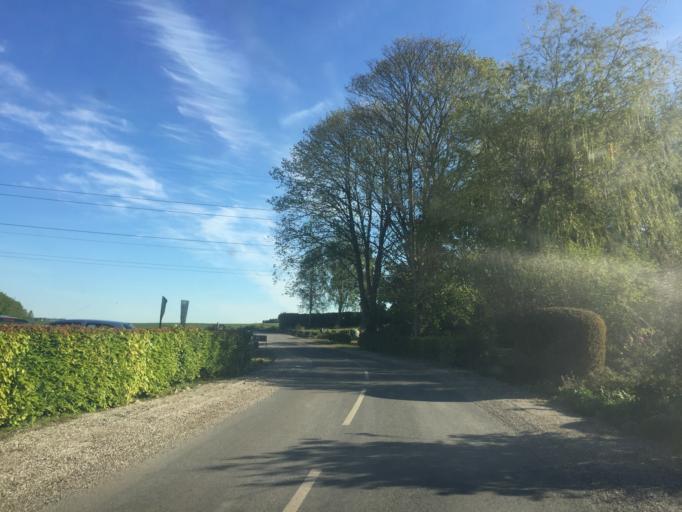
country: DK
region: Capital Region
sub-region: Egedal Kommune
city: Vekso
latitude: 55.7287
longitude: 12.2639
